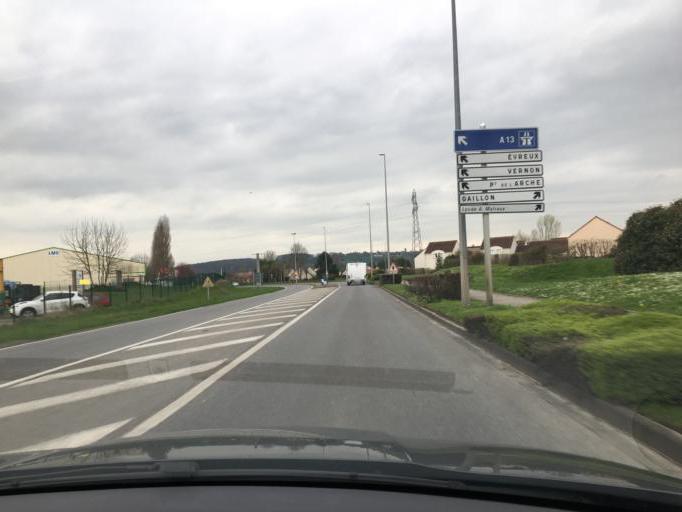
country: FR
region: Haute-Normandie
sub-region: Departement de l'Eure
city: Gaillon
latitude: 49.1689
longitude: 1.3490
